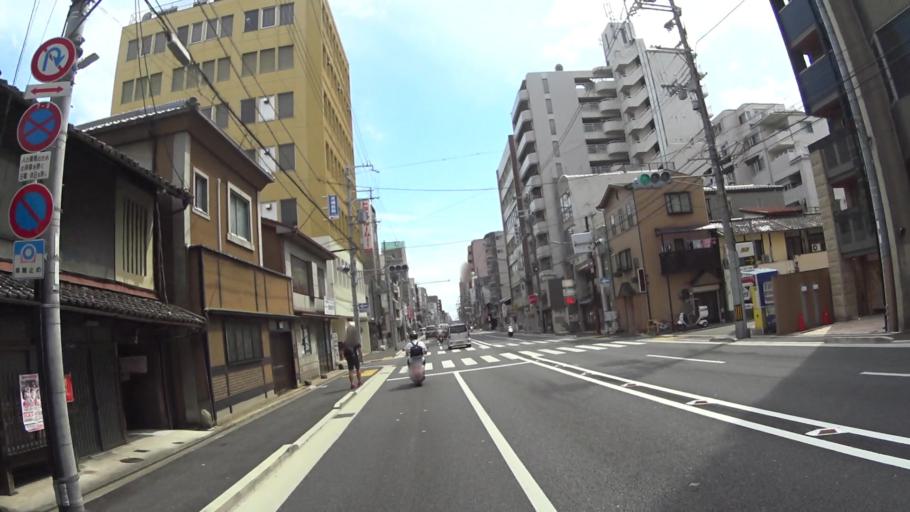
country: JP
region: Kyoto
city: Kyoto
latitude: 35.0015
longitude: 135.7491
